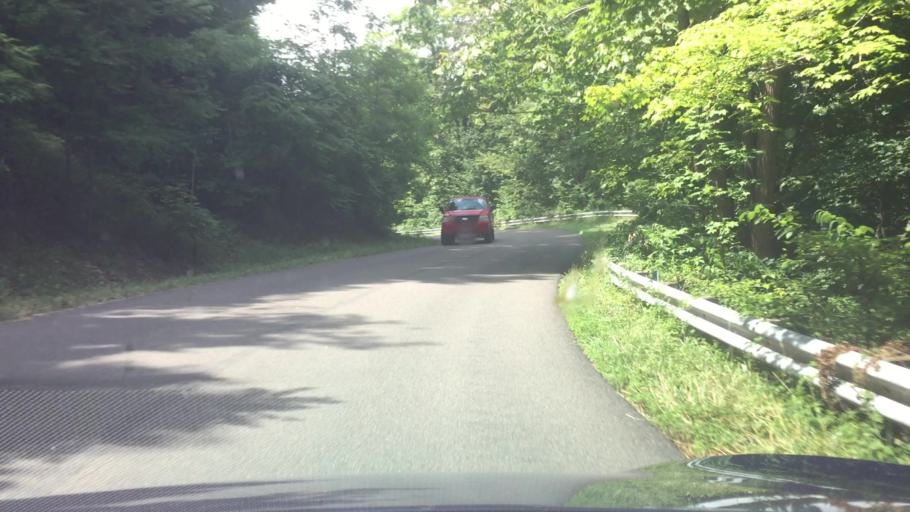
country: US
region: Virginia
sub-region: Wythe County
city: Wytheville
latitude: 36.9296
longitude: -81.0680
